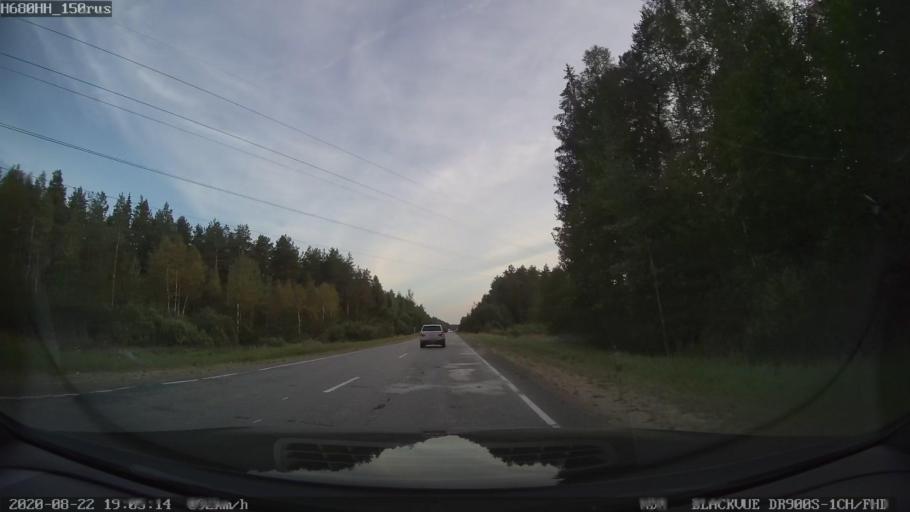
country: RU
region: Tverskaya
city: Sakharovo
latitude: 57.0793
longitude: 36.1127
